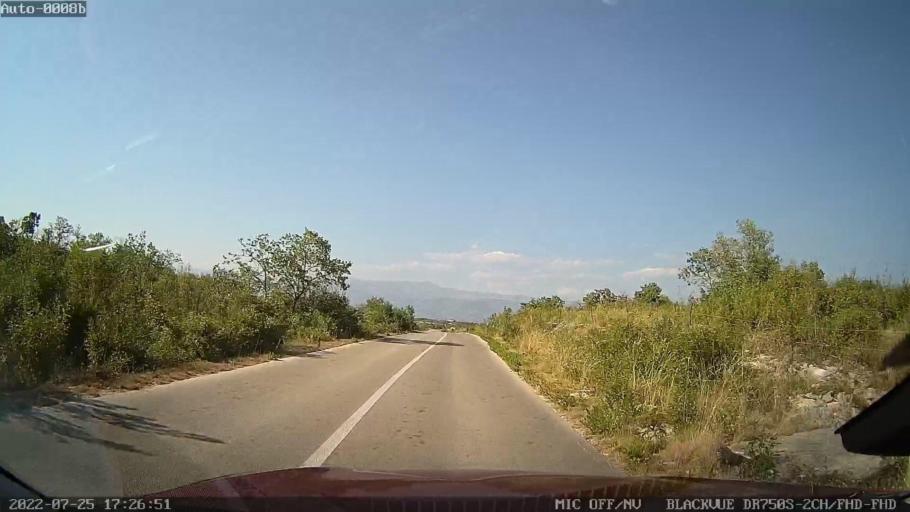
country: HR
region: Zadarska
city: Pridraga
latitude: 44.1376
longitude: 15.5024
